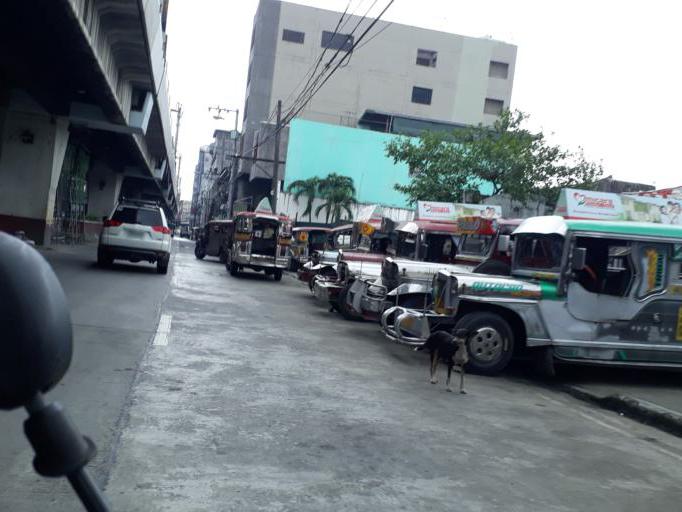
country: PH
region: Metro Manila
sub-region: City of Manila
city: Manila
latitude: 14.6259
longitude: 120.9830
